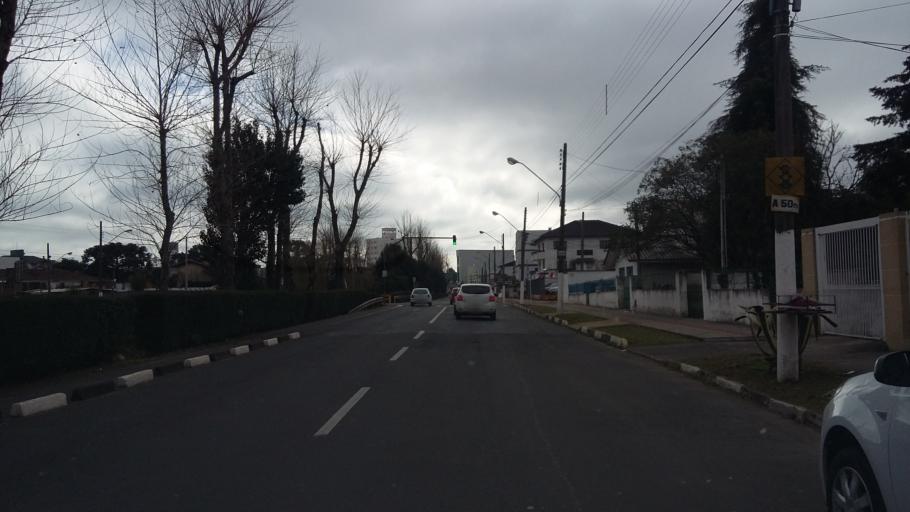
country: BR
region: Santa Catarina
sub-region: Lages
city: Lages
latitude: -27.8161
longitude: -50.3182
